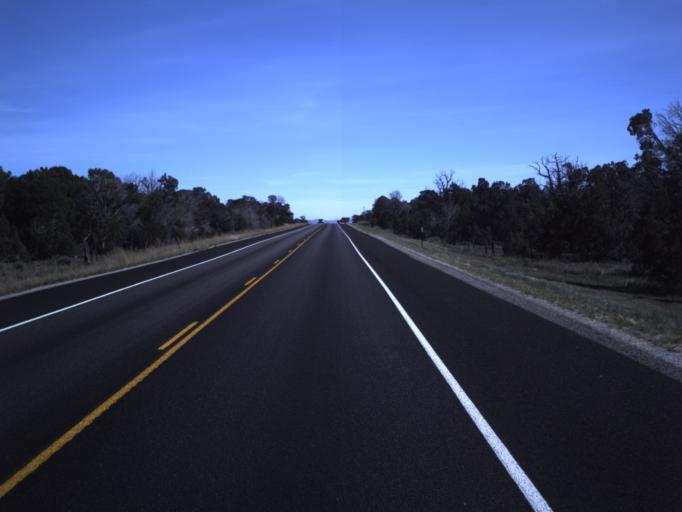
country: US
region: Utah
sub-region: San Juan County
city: Monticello
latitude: 37.8574
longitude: -109.1963
